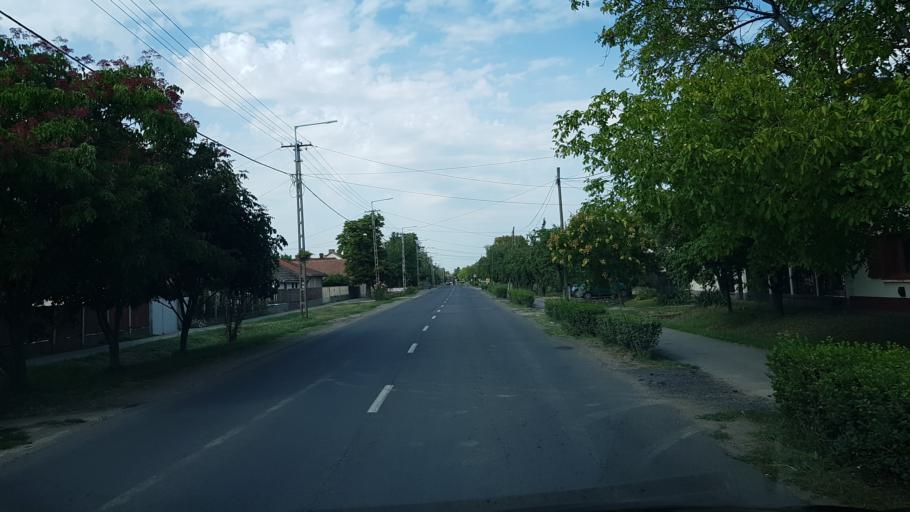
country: HU
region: Bekes
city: Fuzesgyarmat
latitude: 47.0979
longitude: 21.2073
